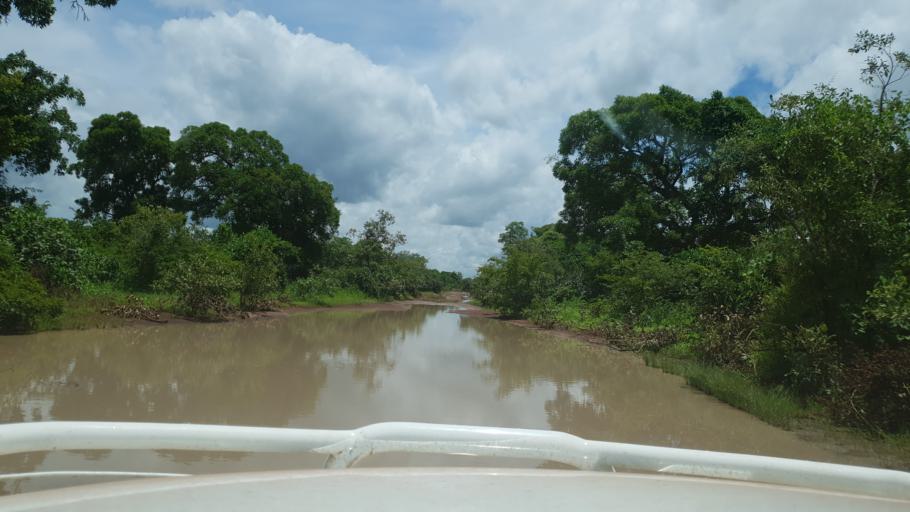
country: ML
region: Koulikoro
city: Banamba
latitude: 13.2004
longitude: -7.3331
